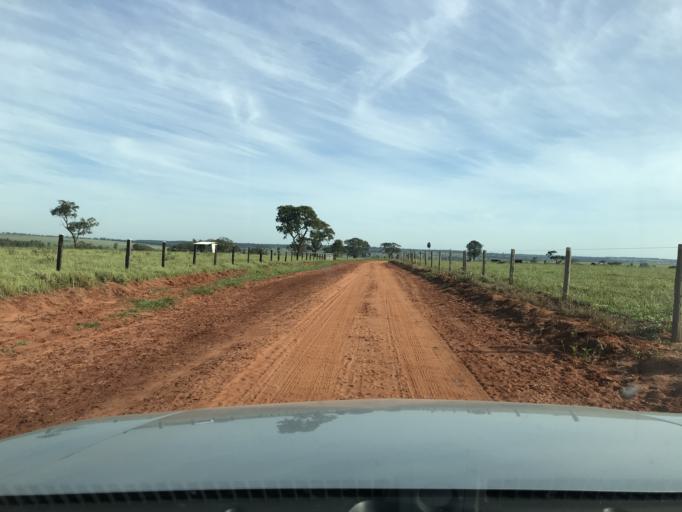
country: BR
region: Mato Grosso do Sul
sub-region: Iguatemi
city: Iguatemi
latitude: -23.6556
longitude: -54.5722
